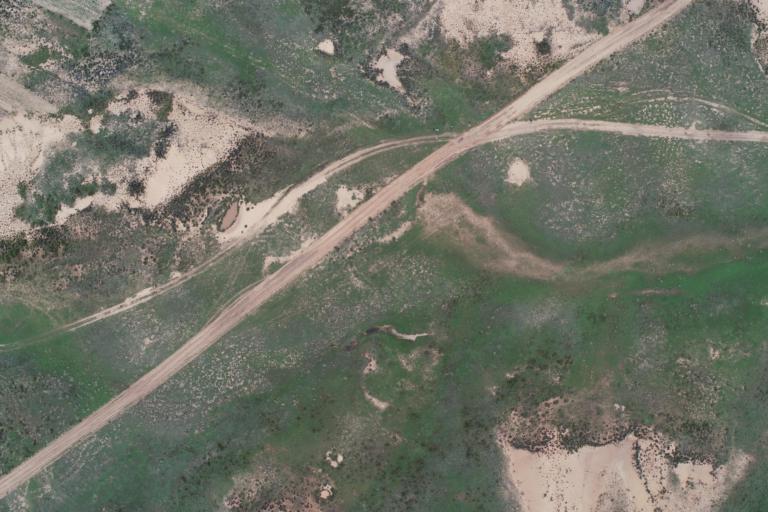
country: BO
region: La Paz
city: Curahuara de Carangas
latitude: -17.2921
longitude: -68.4985
